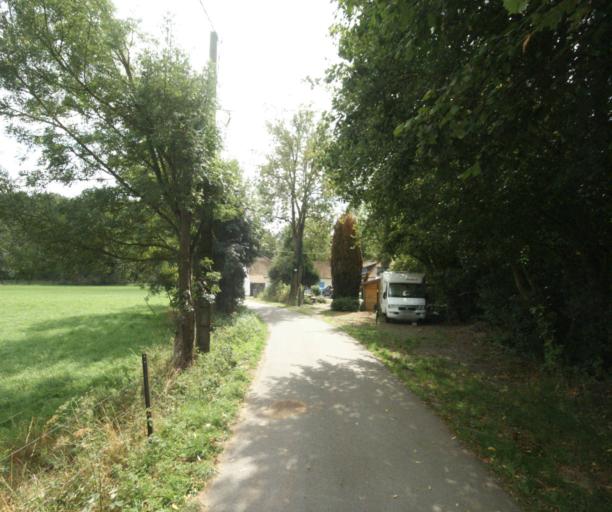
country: FR
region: Nord-Pas-de-Calais
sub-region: Departement du Nord
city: Tressin
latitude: 50.6176
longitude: 3.1978
